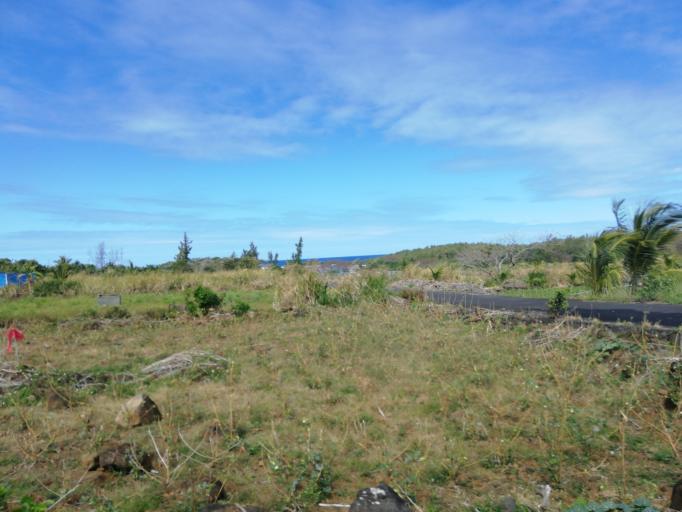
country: MU
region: Grand Port
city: Plaine Magnien
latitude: -20.4655
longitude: 57.6796
